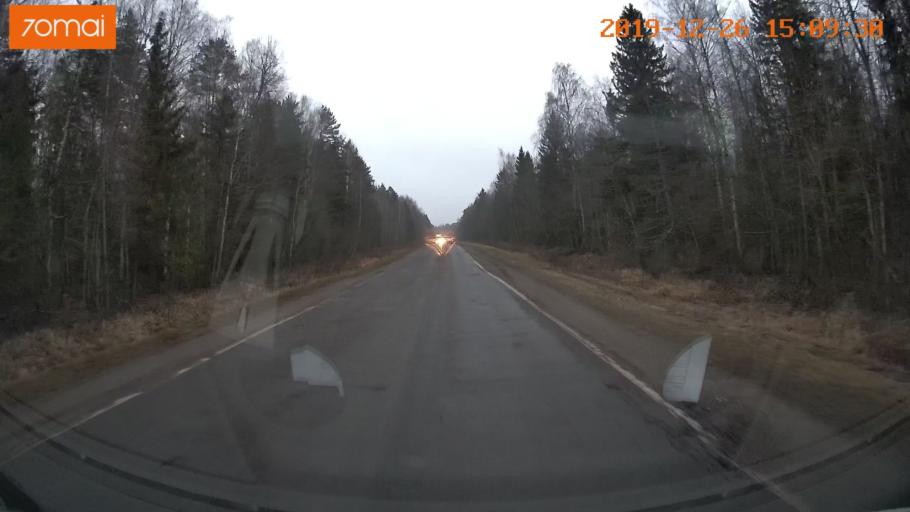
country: RU
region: Jaroslavl
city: Rybinsk
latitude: 58.1484
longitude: 38.8417
